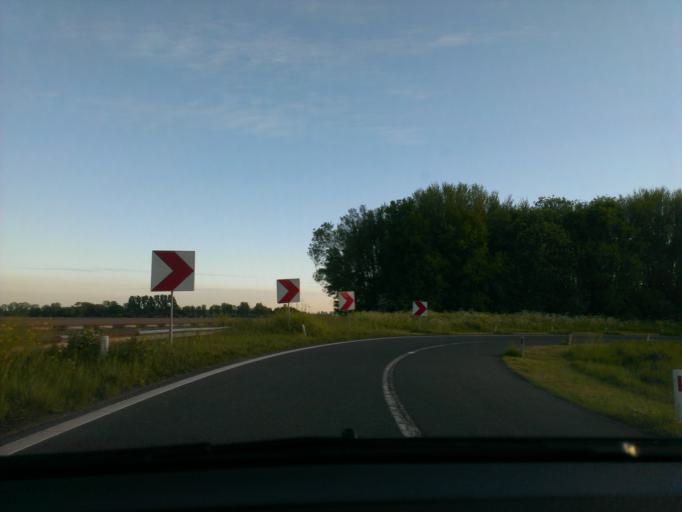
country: NL
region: North Brabant
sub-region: Gemeente Moerdijk
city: Willemstad
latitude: 51.7494
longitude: 4.4167
